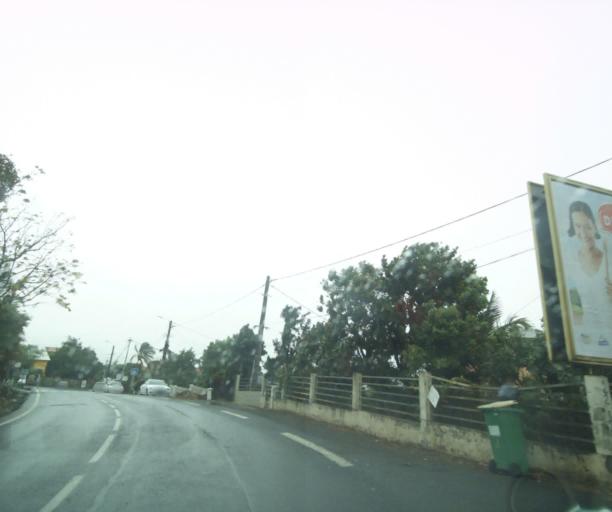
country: RE
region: Reunion
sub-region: Reunion
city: Saint-Paul
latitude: -21.0444
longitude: 55.2636
